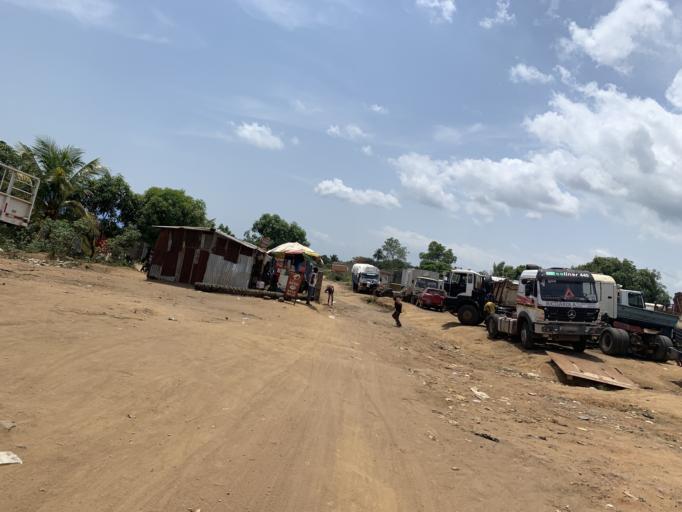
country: SL
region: Western Area
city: Waterloo
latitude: 8.3367
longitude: -13.0249
